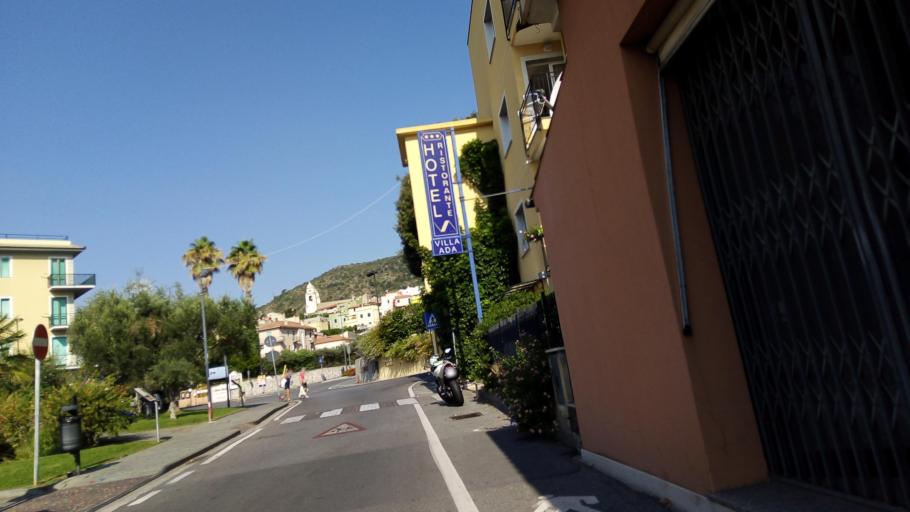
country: IT
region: Liguria
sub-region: Provincia di Savona
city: Borgio
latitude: 44.1596
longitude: 8.3069
